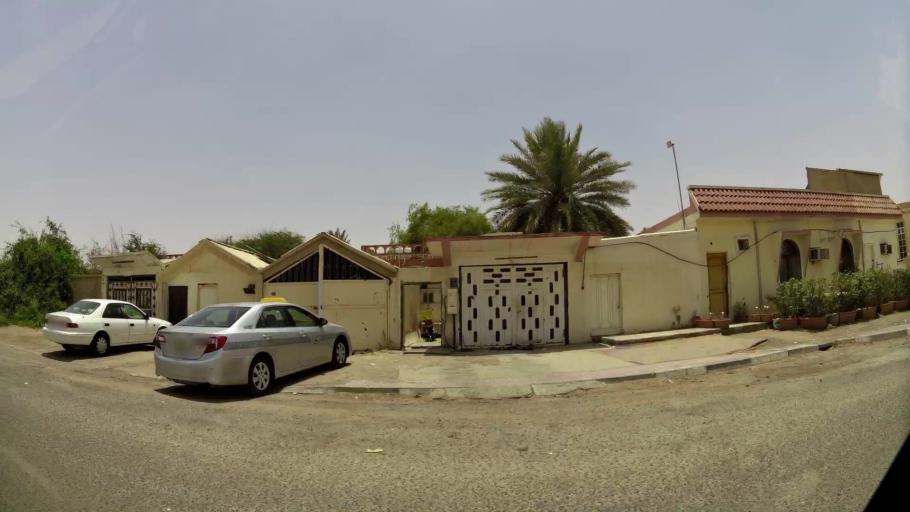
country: AE
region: Abu Dhabi
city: Al Ain
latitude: 24.2146
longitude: 55.7139
